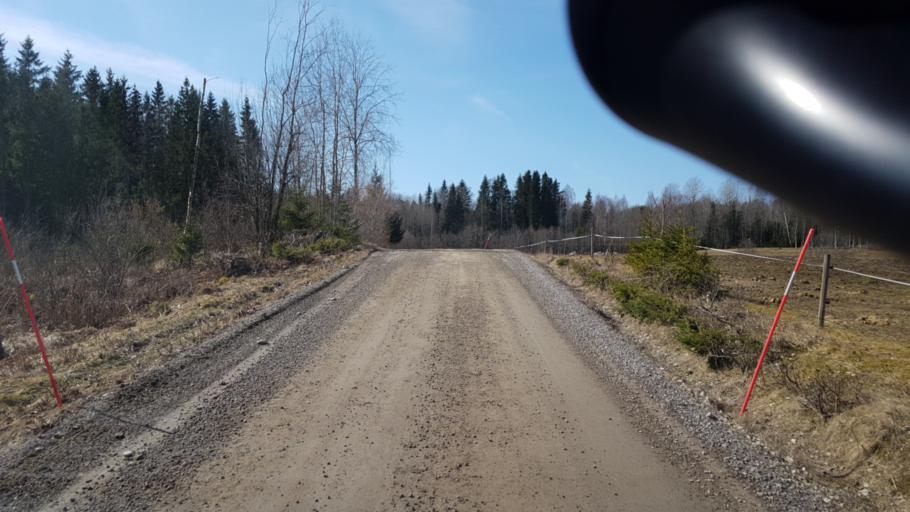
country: SE
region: Vaermland
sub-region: Arvika Kommun
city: Arvika
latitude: 59.5351
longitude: 12.8571
